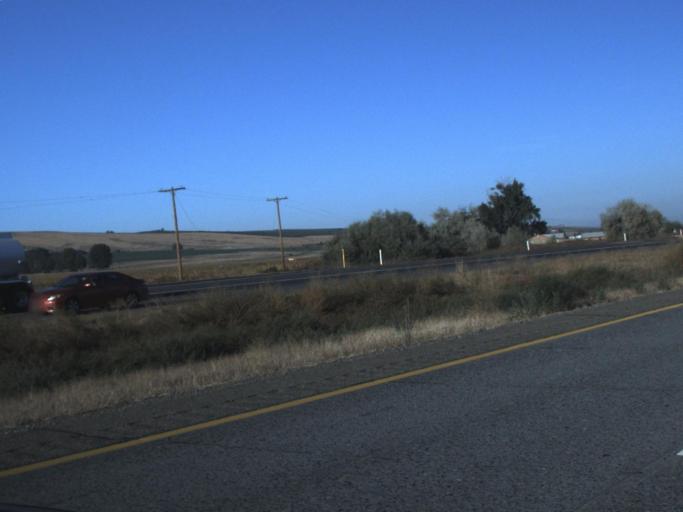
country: US
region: Washington
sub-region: Yakima County
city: Sunnyside
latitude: 46.3242
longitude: -120.0734
